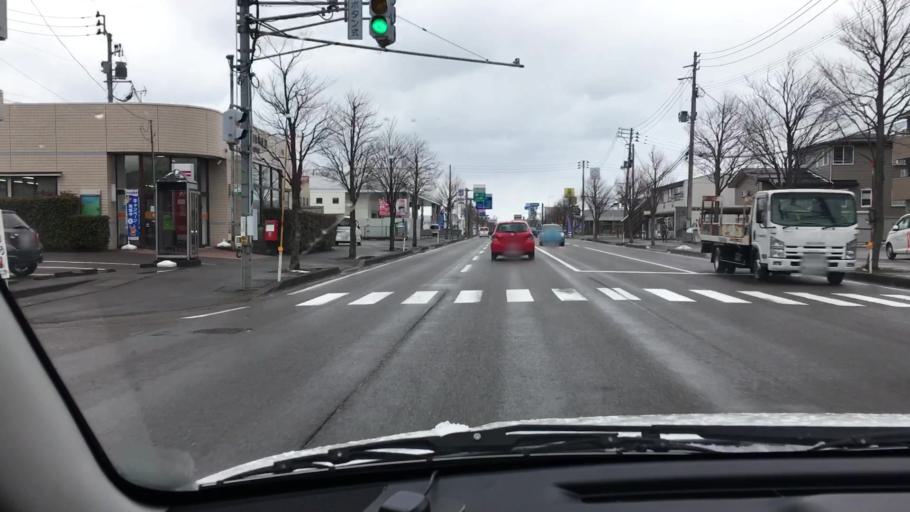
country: JP
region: Niigata
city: Joetsu
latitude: 37.1454
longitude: 138.2284
